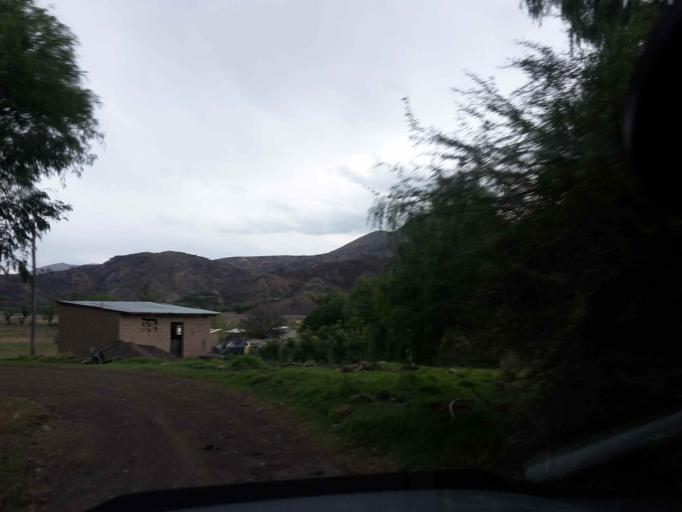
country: BO
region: Cochabamba
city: Sipe Sipe
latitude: -17.5323
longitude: -66.5150
